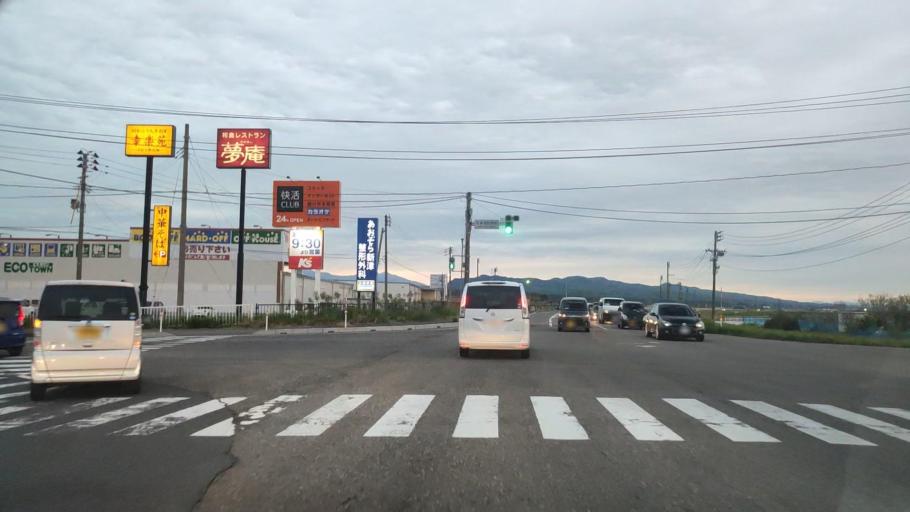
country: JP
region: Niigata
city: Niitsu-honcho
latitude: 37.7865
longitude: 139.1119
